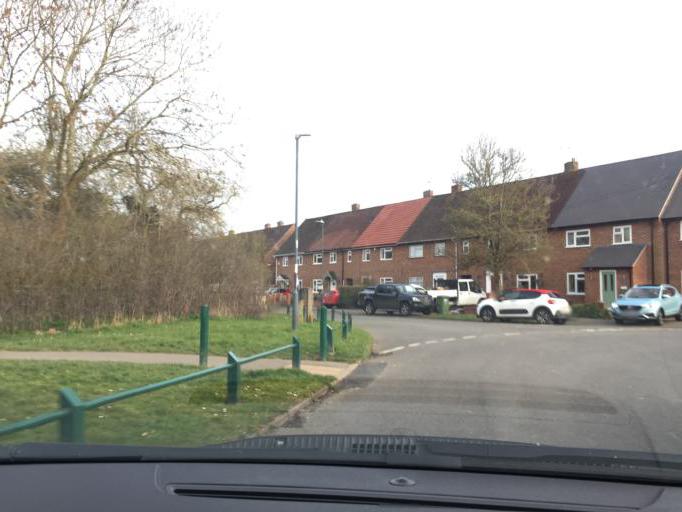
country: GB
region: England
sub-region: Warwickshire
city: Kenilworth
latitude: 52.3348
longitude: -1.5768
